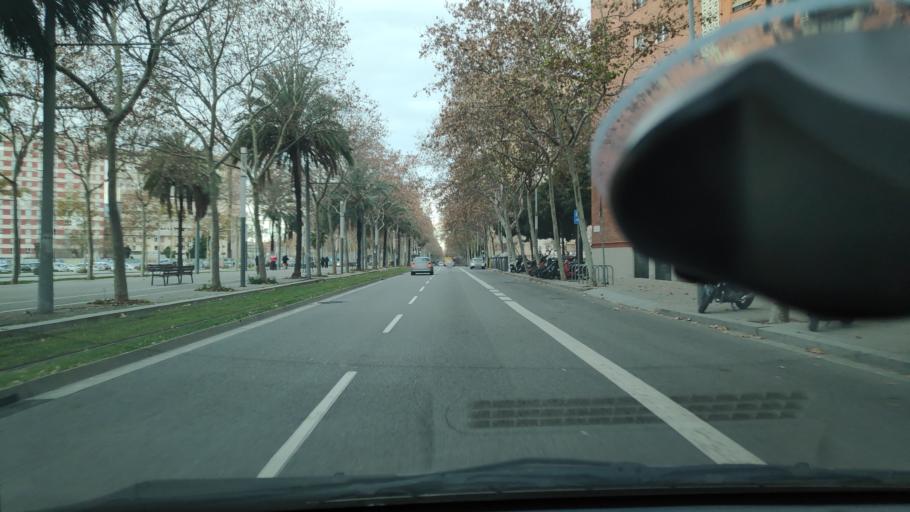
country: ES
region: Catalonia
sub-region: Provincia de Barcelona
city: Sant Marti
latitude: 41.4098
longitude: 2.2124
